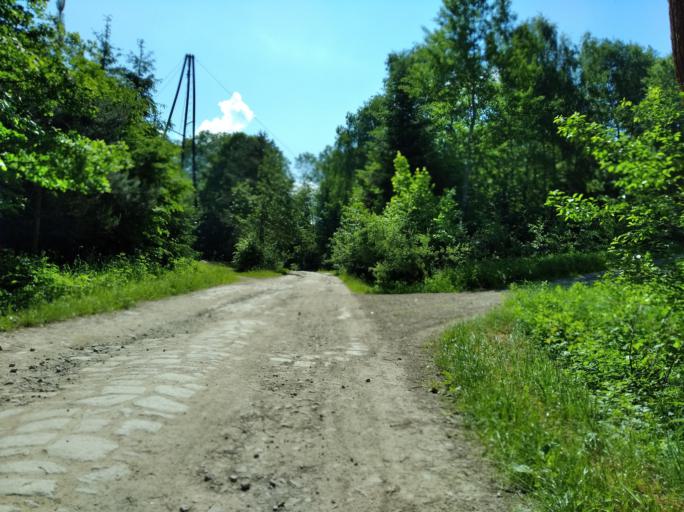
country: PL
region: Subcarpathian Voivodeship
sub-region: Powiat krosnienski
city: Odrzykon
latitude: 49.7702
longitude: 21.7682
